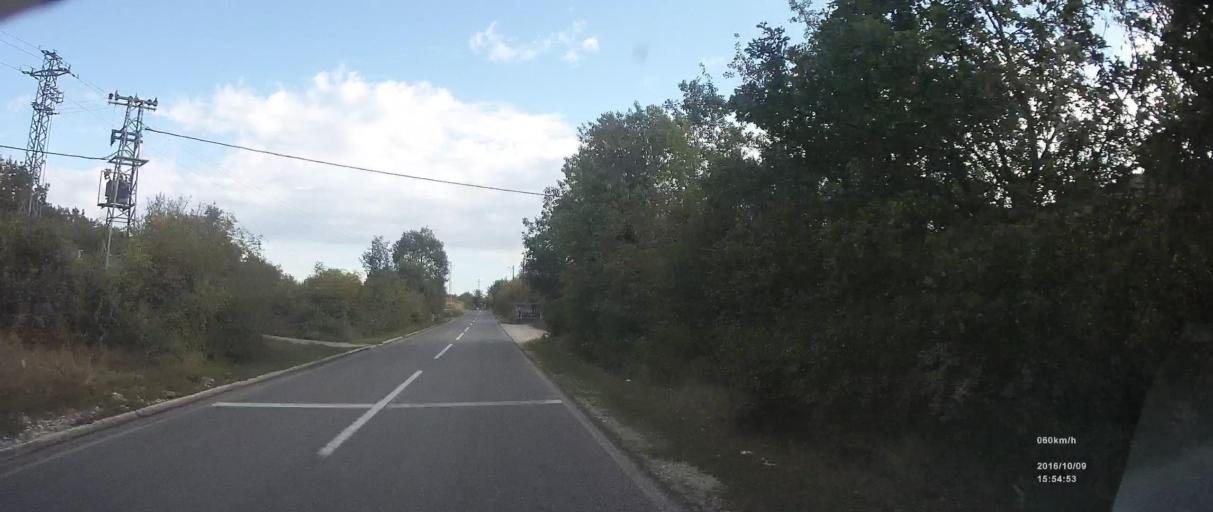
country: HR
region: Splitsko-Dalmatinska
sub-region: Grad Trogir
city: Trogir
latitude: 43.5909
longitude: 16.2266
